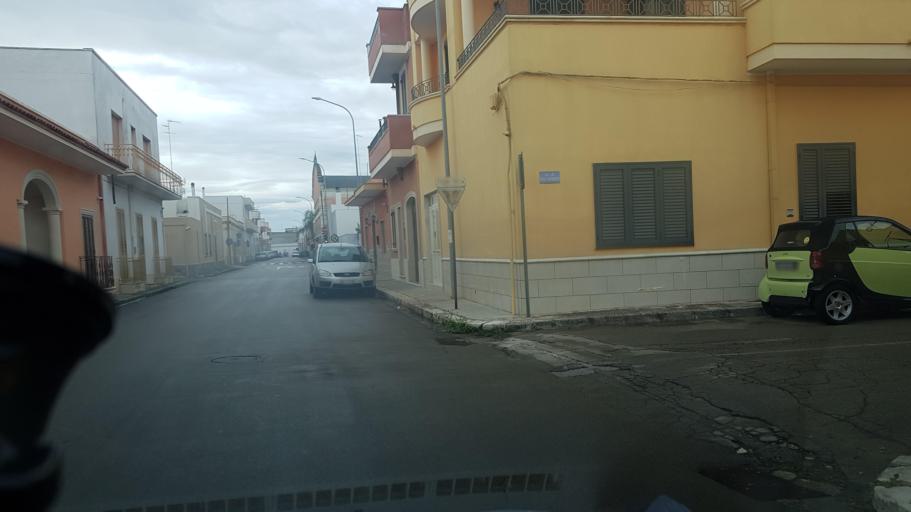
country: IT
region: Apulia
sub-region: Provincia di Lecce
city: Salice Salentino
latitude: 40.3816
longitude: 17.9670
